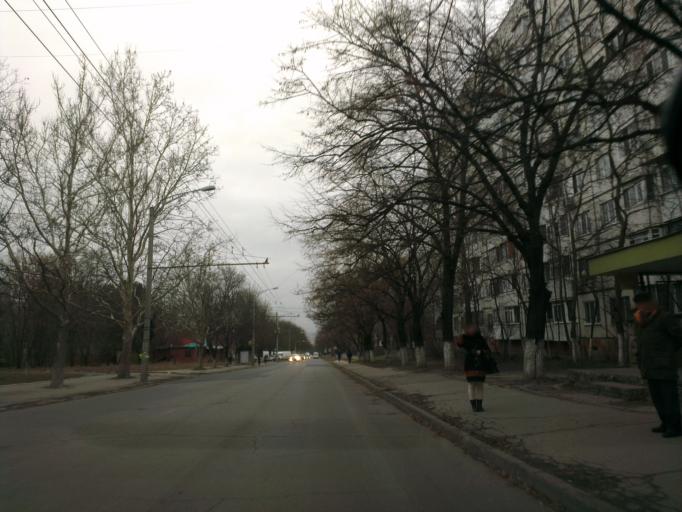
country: MD
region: Chisinau
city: Chisinau
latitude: 46.9891
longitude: 28.8452
